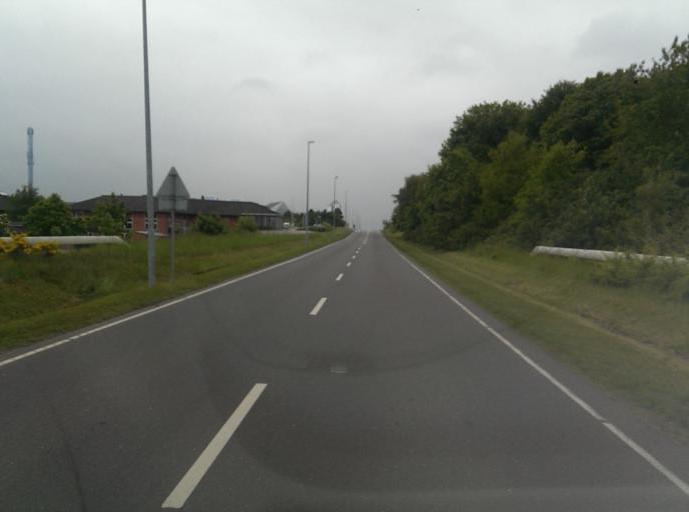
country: DK
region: South Denmark
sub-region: Fano Kommune
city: Nordby
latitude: 55.5285
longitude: 8.3582
